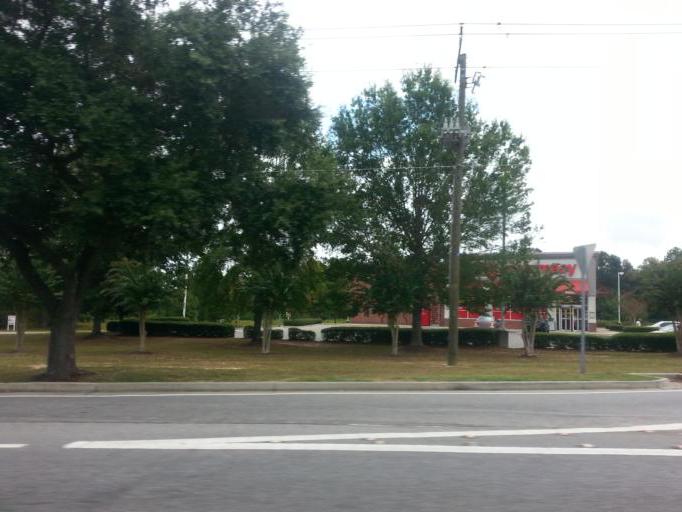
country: US
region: Alabama
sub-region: Baldwin County
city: Daphne
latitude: 30.6189
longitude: -87.9053
